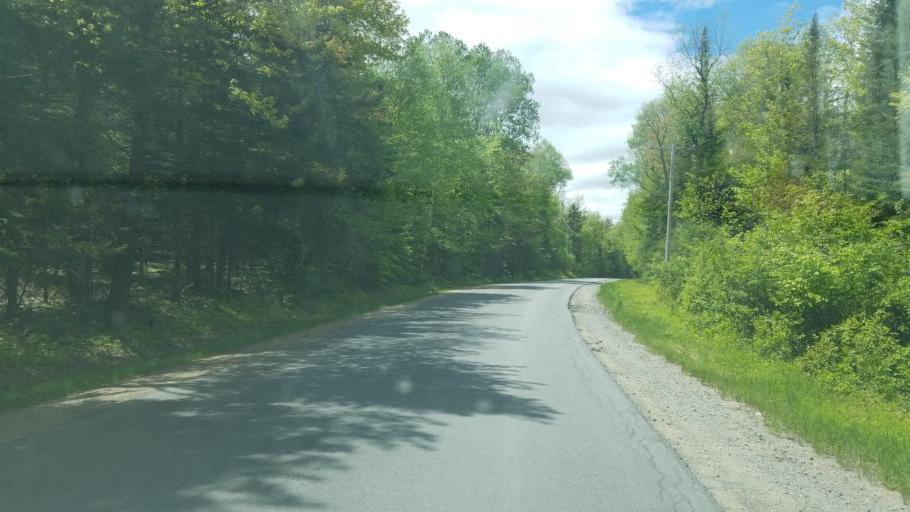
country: US
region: New York
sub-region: Hamilton County
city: Lake Pleasant
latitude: 43.7839
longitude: -74.3136
